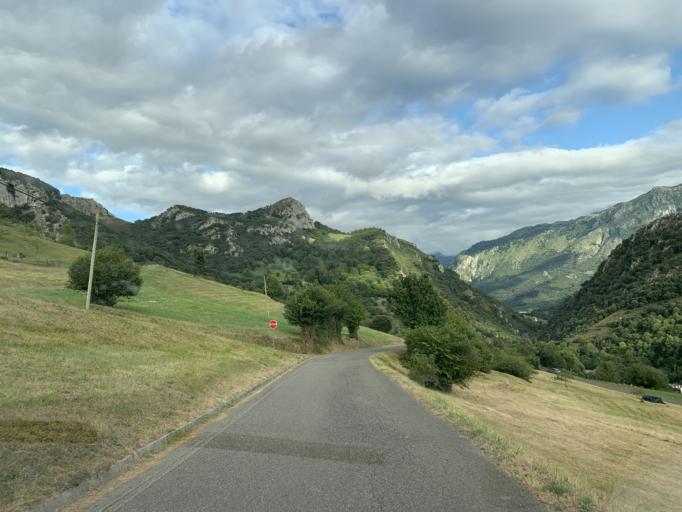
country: ES
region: Asturias
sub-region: Province of Asturias
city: Carrena
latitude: 43.3189
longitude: -4.8520
